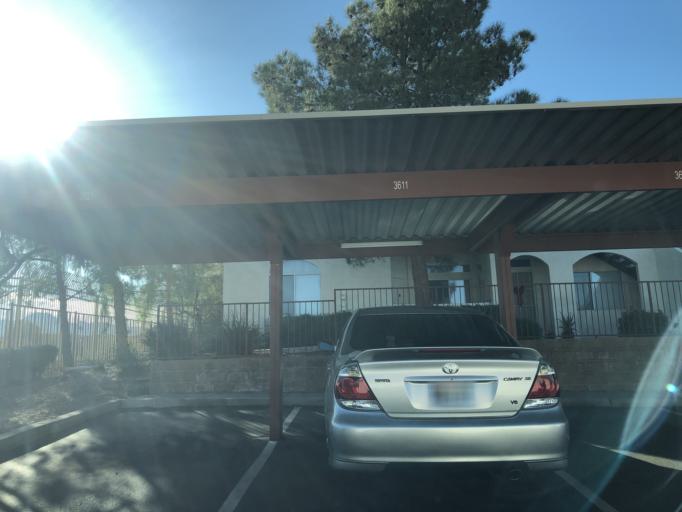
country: US
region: Nevada
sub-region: Clark County
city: Whitney
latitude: 36.0045
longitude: -115.0925
